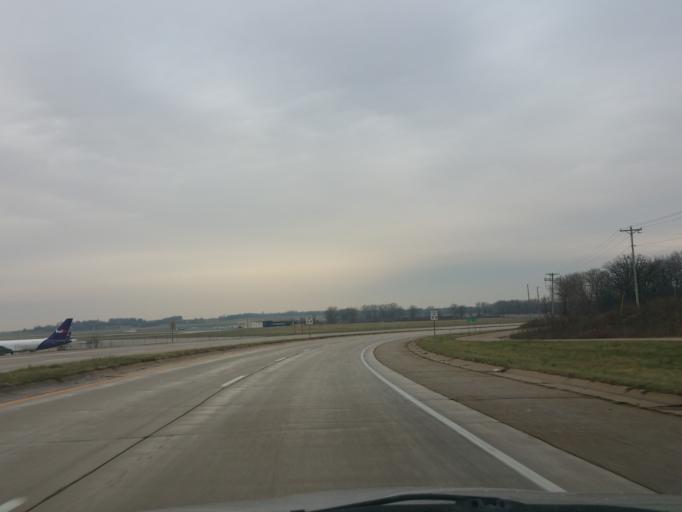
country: US
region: Wisconsin
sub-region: Dane County
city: Maple Bluff
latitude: 43.1295
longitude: -89.3252
